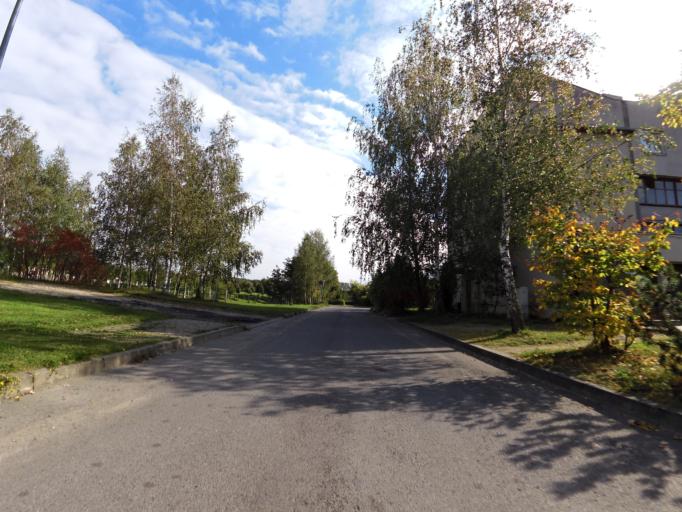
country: LT
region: Vilnius County
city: Pilaite
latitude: 54.7014
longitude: 25.1722
